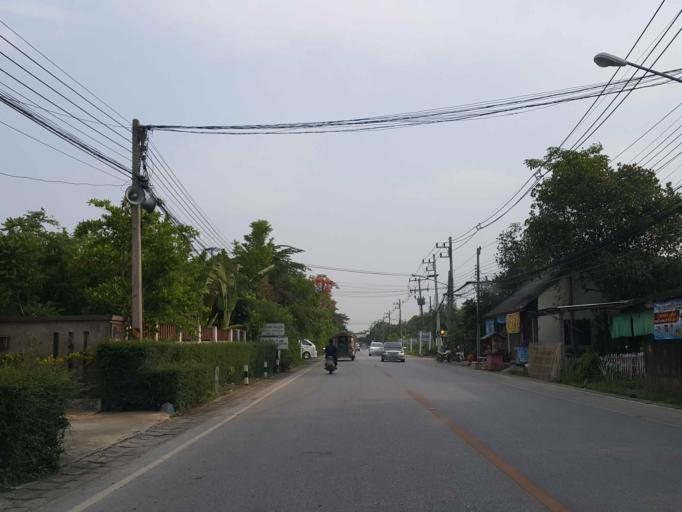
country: TH
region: Chiang Mai
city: San Kamphaeng
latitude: 18.8152
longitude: 99.1221
